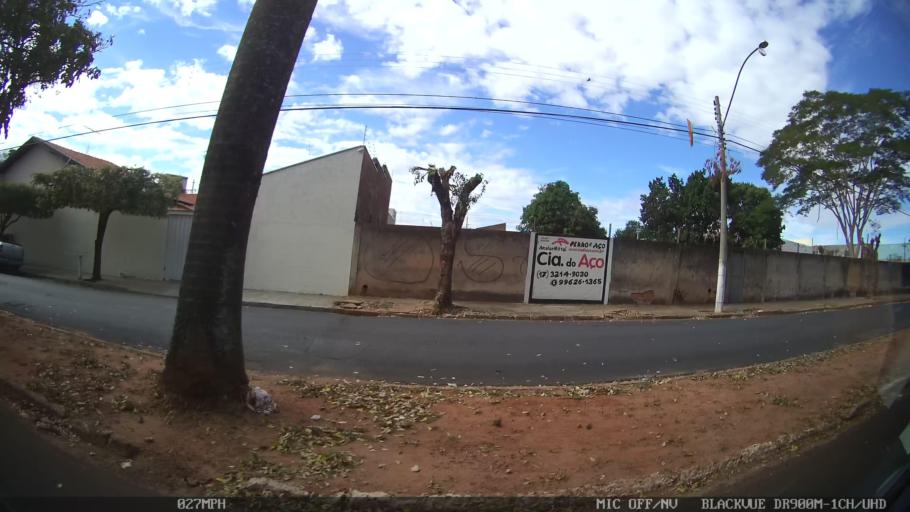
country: BR
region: Sao Paulo
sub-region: Bady Bassitt
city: Bady Bassitt
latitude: -20.8177
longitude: -49.5233
